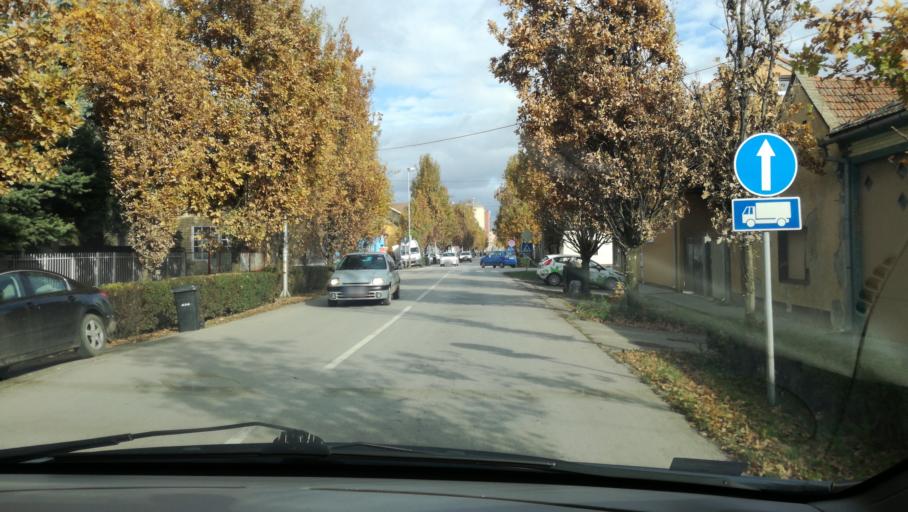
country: RS
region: Autonomna Pokrajina Vojvodina
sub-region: Severnobanatski Okrug
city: Kikinda
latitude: 45.8294
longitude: 20.4601
